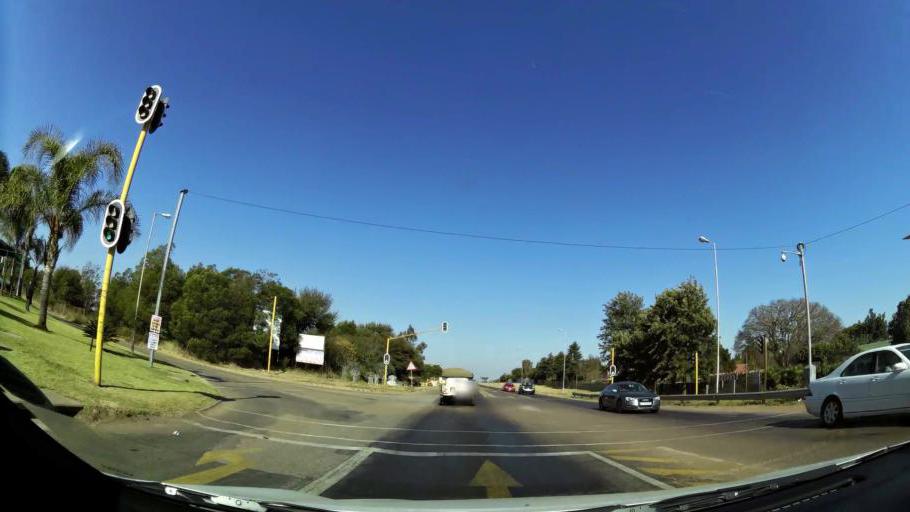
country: ZA
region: Gauteng
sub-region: City of Tshwane Metropolitan Municipality
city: Centurion
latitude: -25.8376
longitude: 28.2701
